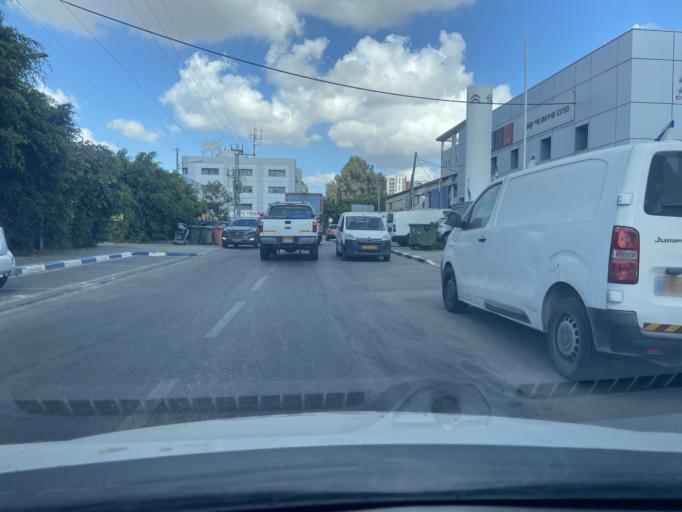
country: IL
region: Central District
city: Yehud
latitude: 32.0273
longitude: 34.8947
